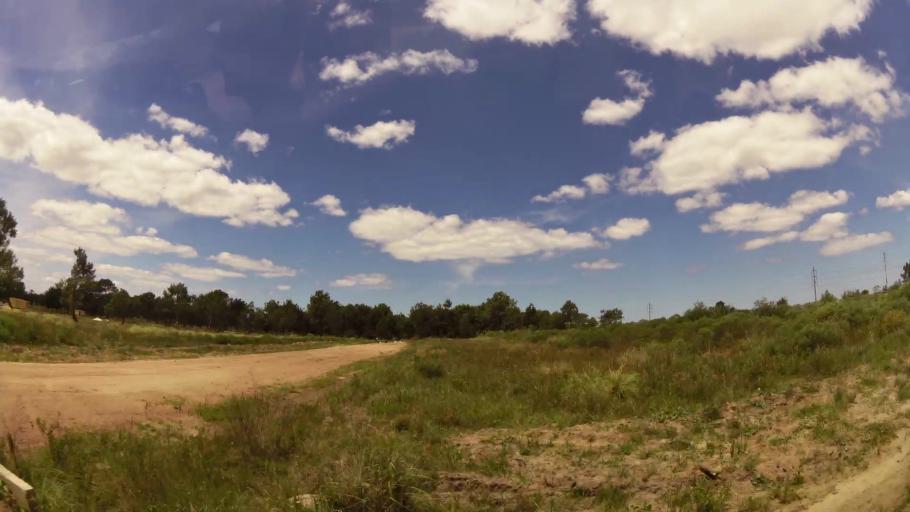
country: UY
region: Canelones
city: Pando
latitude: -34.8080
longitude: -55.9441
